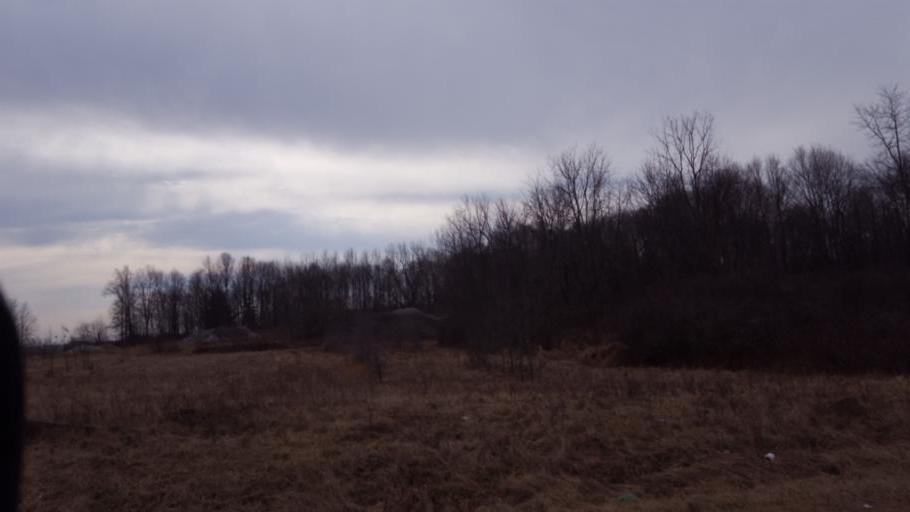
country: US
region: Ohio
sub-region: Richland County
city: Mansfield
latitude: 40.8059
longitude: -82.5339
